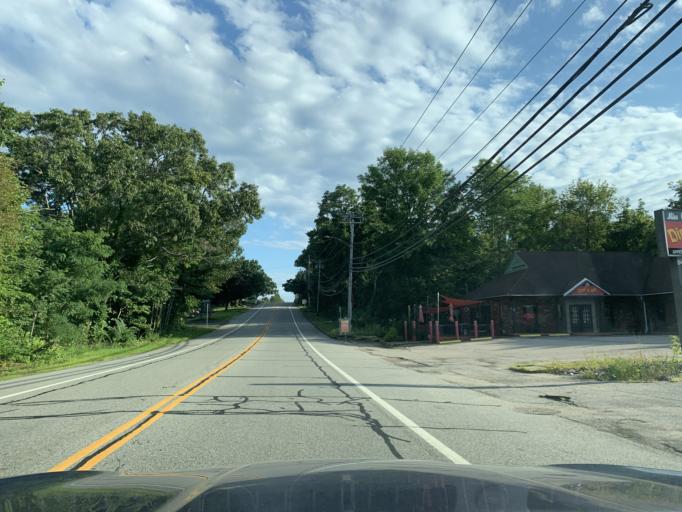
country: US
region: Rhode Island
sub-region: Kent County
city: West Warwick
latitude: 41.6954
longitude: -71.5016
